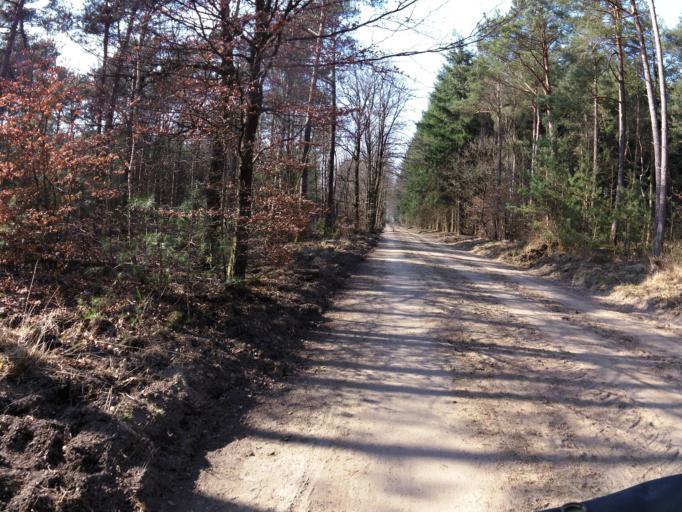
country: NL
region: Gelderland
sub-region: Gemeente Epe
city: Epe
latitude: 52.3663
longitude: 5.9475
